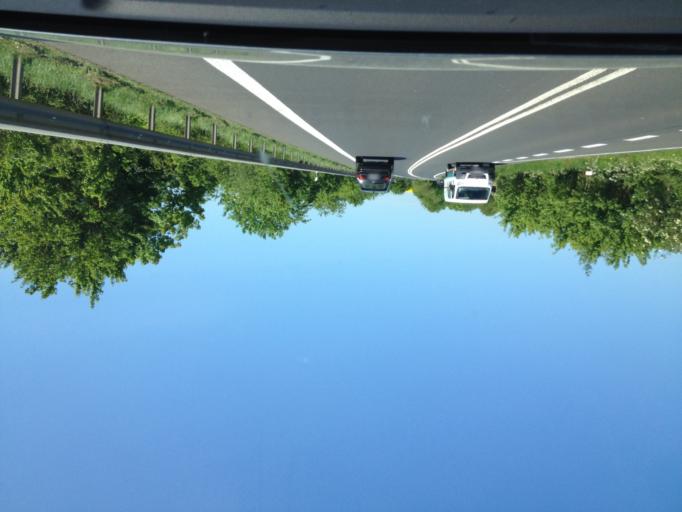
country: DE
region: Rheinland-Pfalz
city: Fliessem
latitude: 49.9981
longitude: 6.5348
